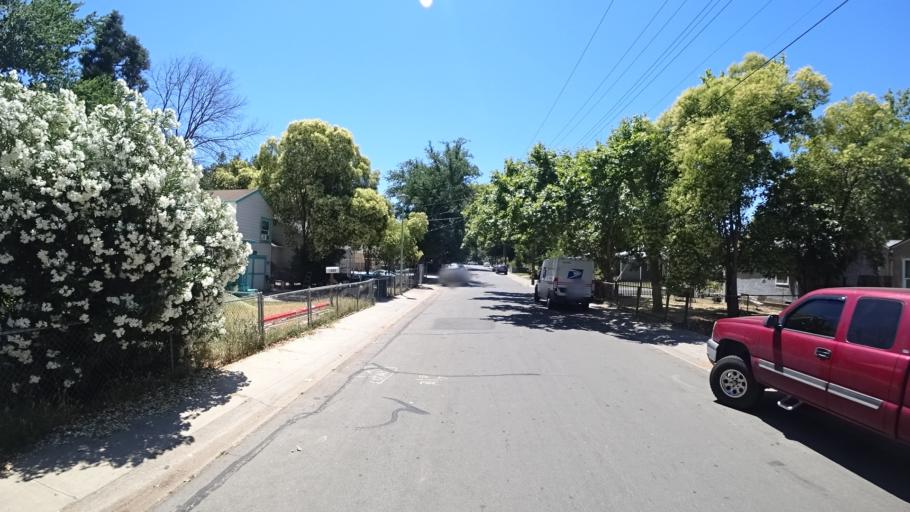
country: US
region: California
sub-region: Sacramento County
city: Sacramento
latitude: 38.5429
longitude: -121.4681
